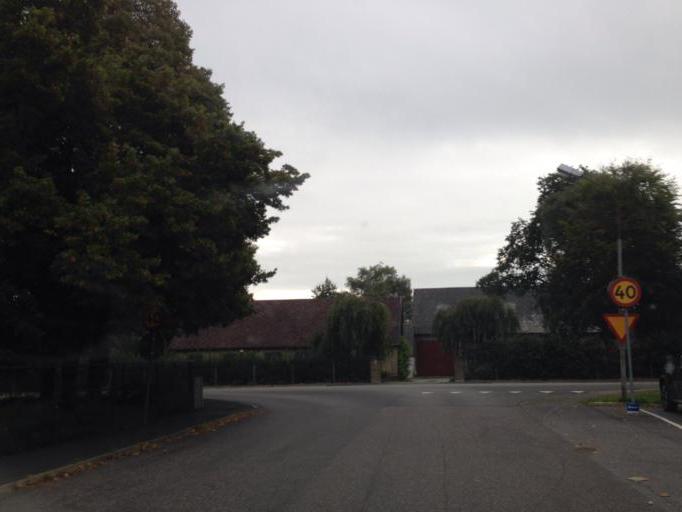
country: SE
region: Skane
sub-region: Lomma Kommun
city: Lomma
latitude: 55.6740
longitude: 13.0866
